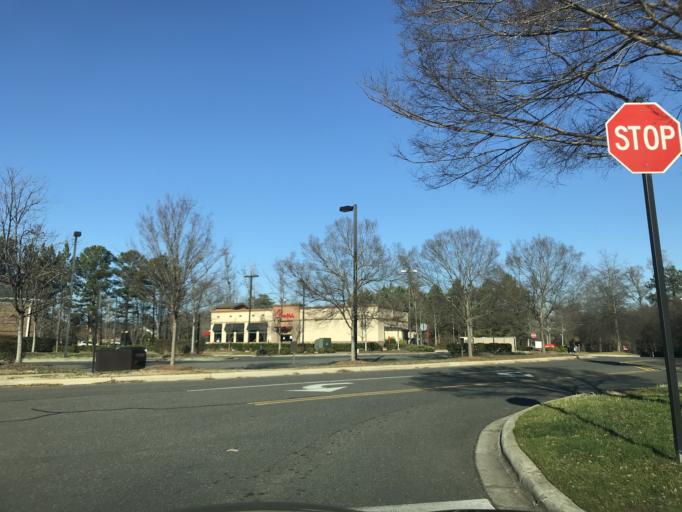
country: US
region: North Carolina
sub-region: Wake County
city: Morrisville
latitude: 35.9003
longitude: -78.7910
